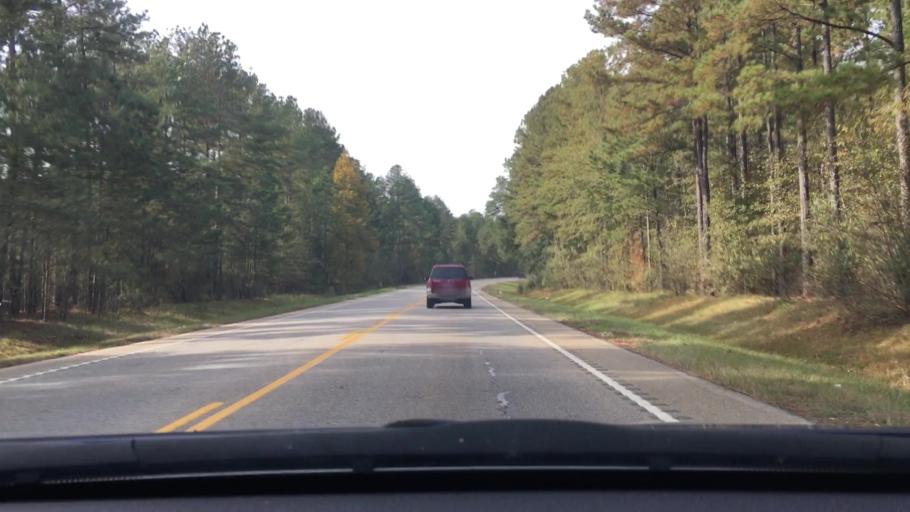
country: US
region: South Carolina
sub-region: Sumter County
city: Cherryvale
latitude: 33.9424
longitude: -80.4887
